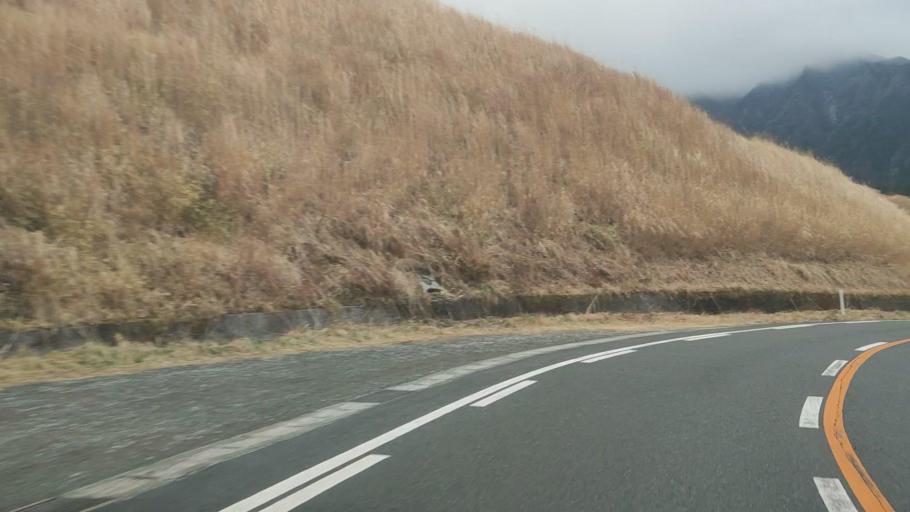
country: JP
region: Kumamoto
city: Aso
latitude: 32.9034
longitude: 131.1526
